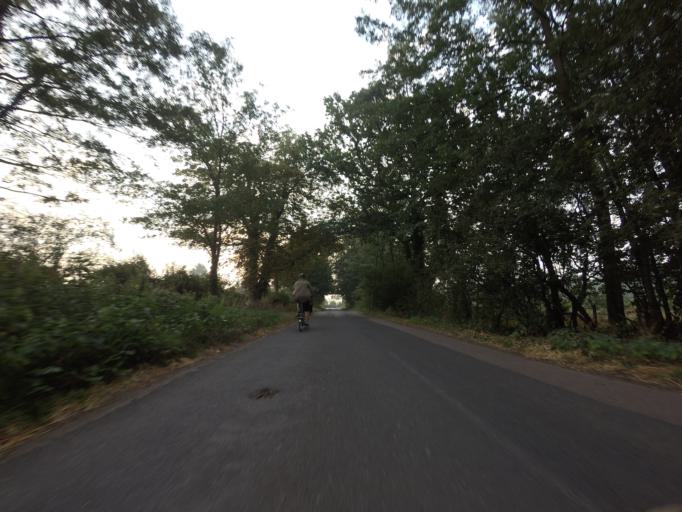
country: GB
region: England
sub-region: Kent
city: Lenham
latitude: 51.1603
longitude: 0.7446
